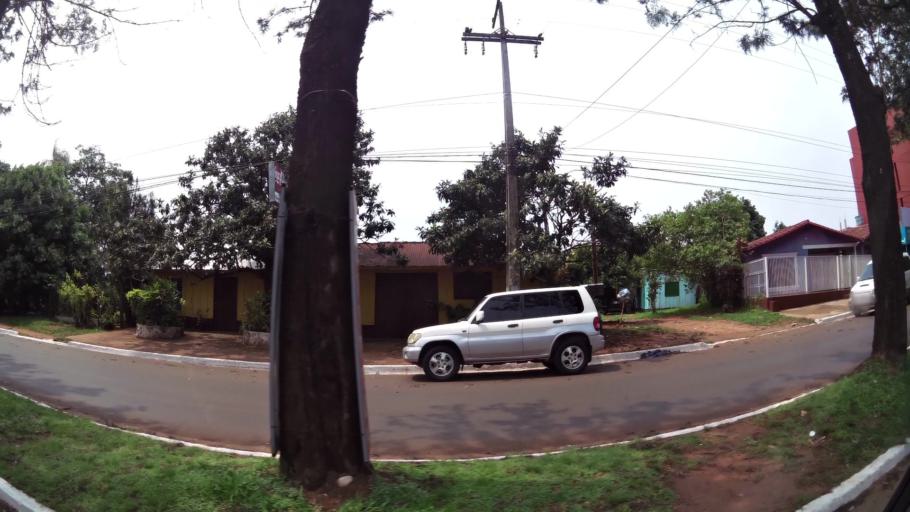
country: BR
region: Parana
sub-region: Foz Do Iguacu
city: Foz do Iguacu
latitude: -25.5604
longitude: -54.6079
